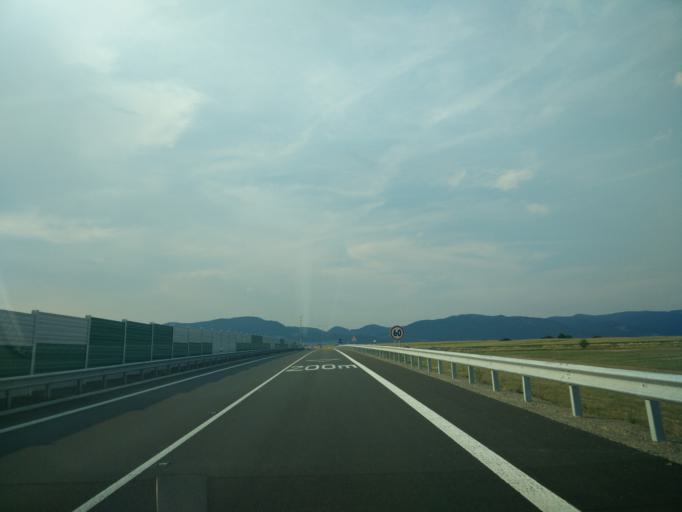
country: SK
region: Banskobystricky
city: Ziar nad Hronom
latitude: 48.6181
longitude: 18.8030
